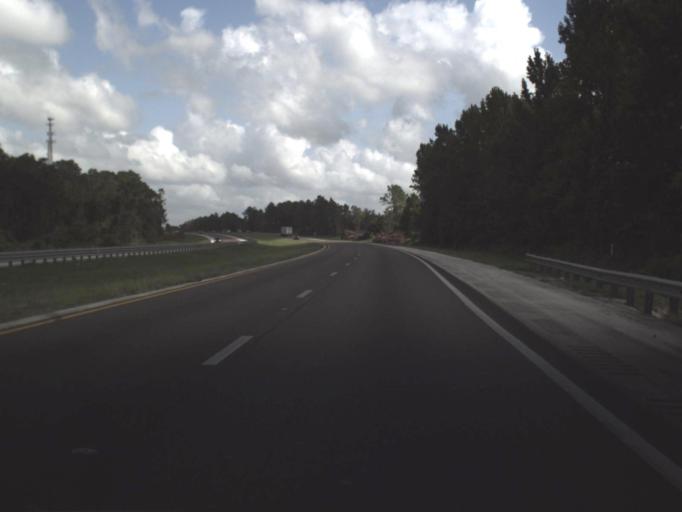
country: US
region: Florida
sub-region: Pasco County
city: Wesley Chapel
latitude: 28.2734
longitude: -82.3270
